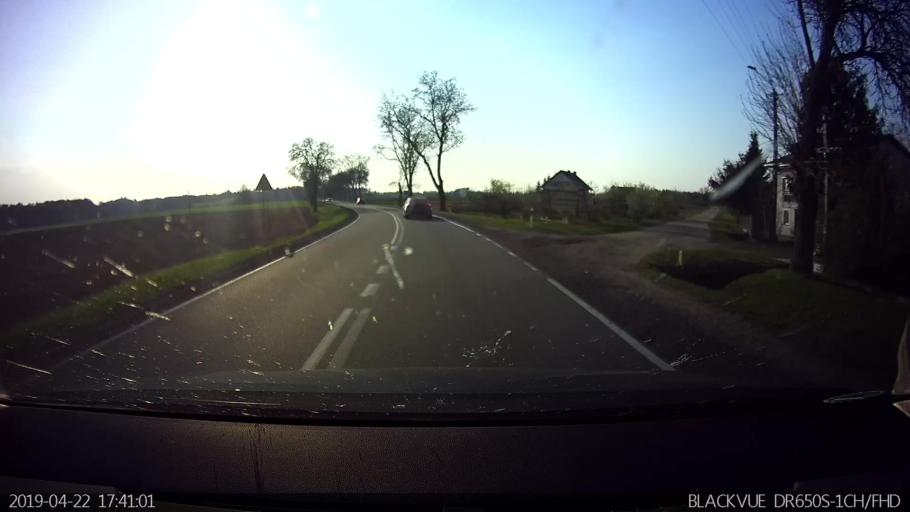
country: PL
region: Masovian Voivodeship
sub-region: Powiat wegrowski
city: Miedzna
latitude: 52.4012
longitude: 22.1168
